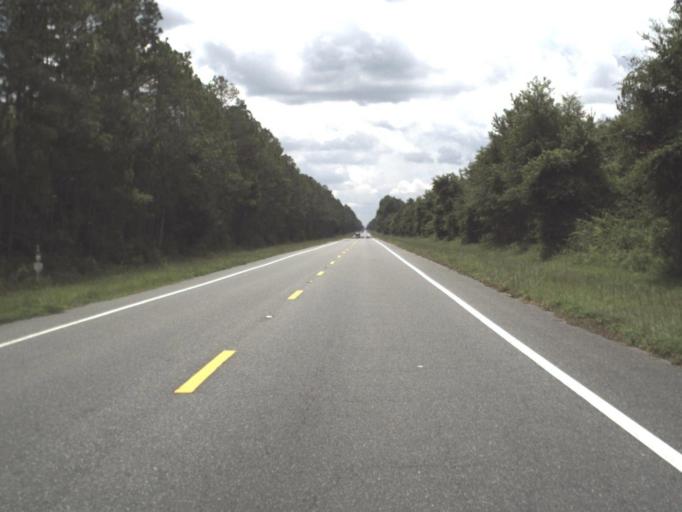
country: US
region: Florida
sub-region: Columbia County
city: Watertown
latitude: 30.1459
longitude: -82.5459
